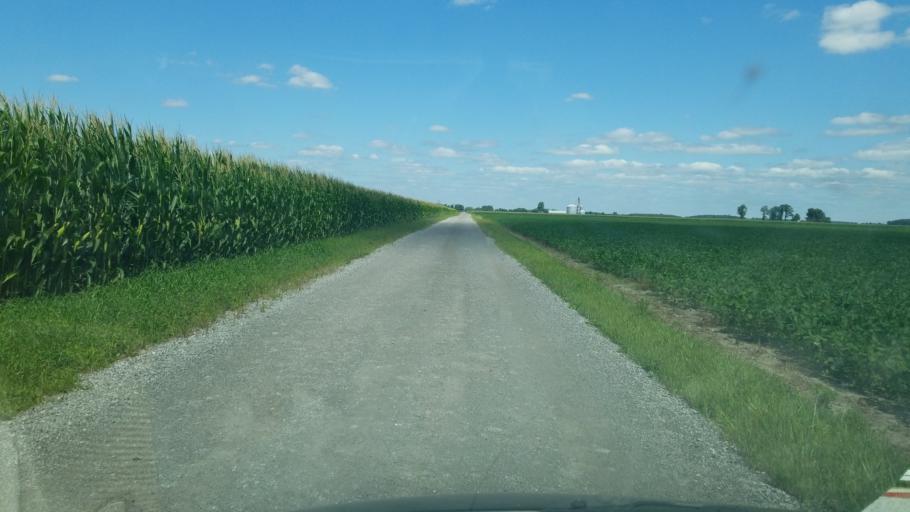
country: US
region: Ohio
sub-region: Fulton County
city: Delta
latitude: 41.6731
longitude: -84.0165
